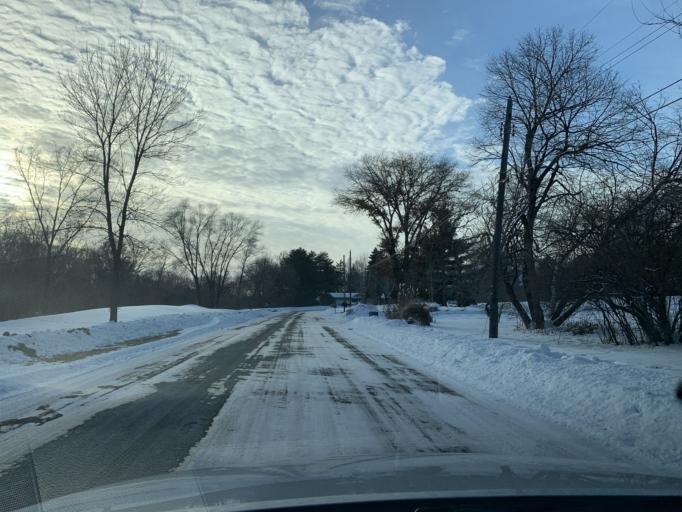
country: US
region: Minnesota
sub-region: Hennepin County
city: Minnetonka Mills
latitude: 44.9509
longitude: -93.3974
